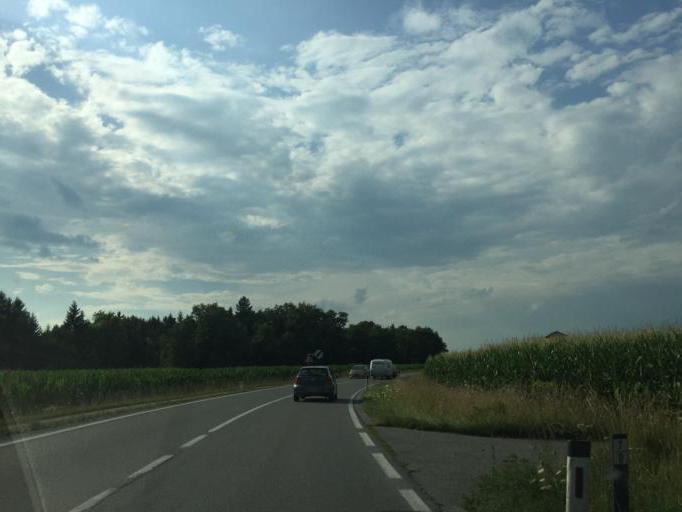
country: AT
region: Styria
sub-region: Politischer Bezirk Suedoststeiermark
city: Weinburg am Sassbach
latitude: 46.7413
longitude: 15.7196
